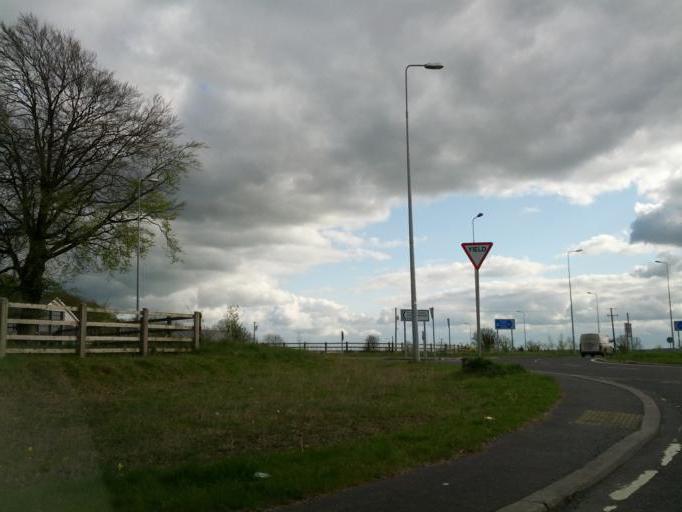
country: IE
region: Connaught
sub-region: County Galway
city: Ballinasloe
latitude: 53.3204
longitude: -8.1799
